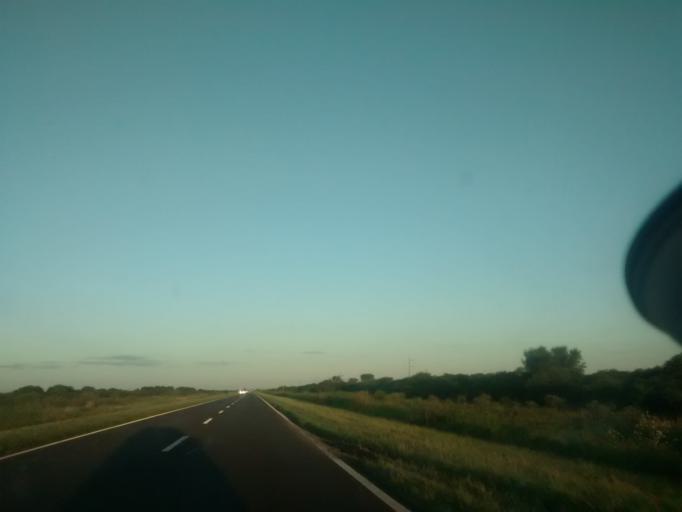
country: AR
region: Chaco
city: La Escondida
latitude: -27.1210
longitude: -59.5422
